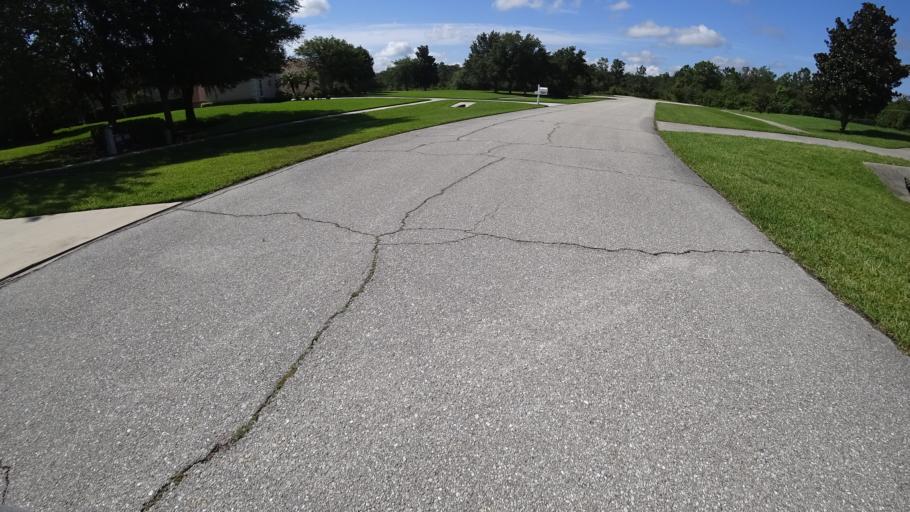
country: US
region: Florida
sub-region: Sarasota County
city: Fruitville
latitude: 27.3884
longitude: -82.3118
